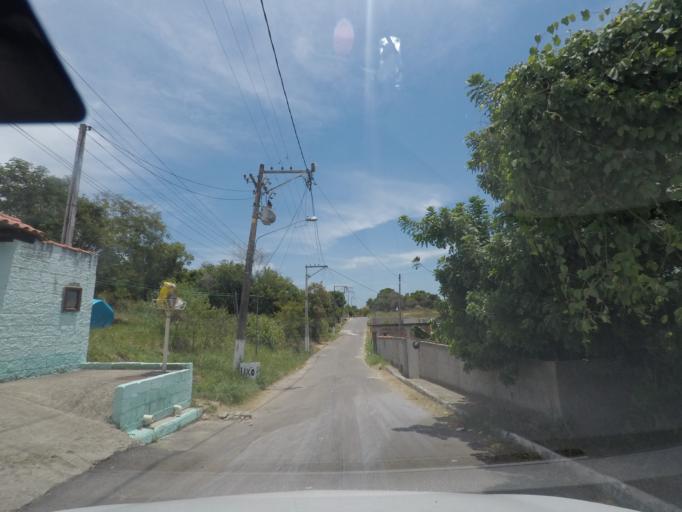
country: BR
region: Rio de Janeiro
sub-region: Marica
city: Marica
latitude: -22.9305
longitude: -42.8250
